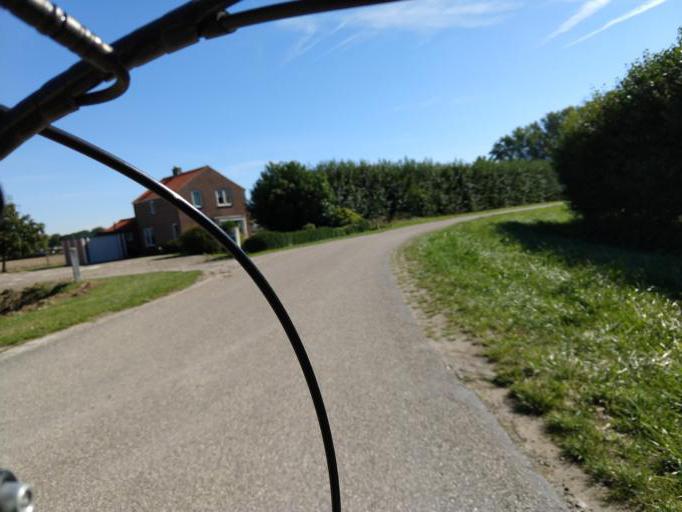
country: NL
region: Zeeland
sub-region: Gemeente Terneuzen
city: Terneuzen
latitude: 51.4089
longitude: 3.8392
